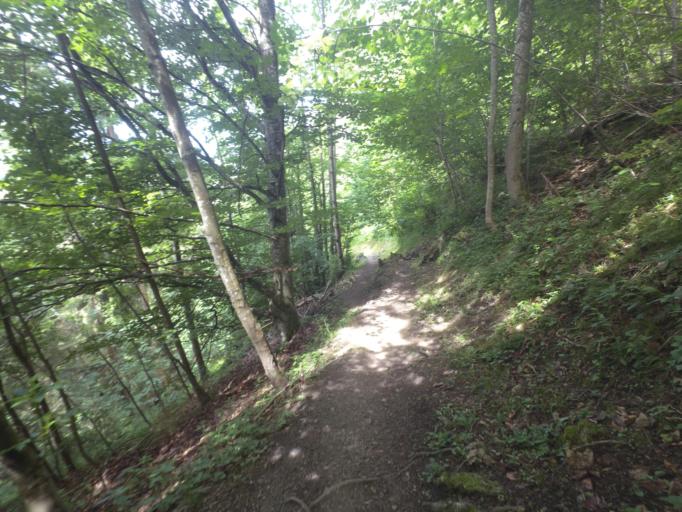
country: AT
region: Salzburg
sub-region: Politischer Bezirk Zell am See
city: Saalfelden am Steinernen Meer
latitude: 47.4440
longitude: 12.8592
